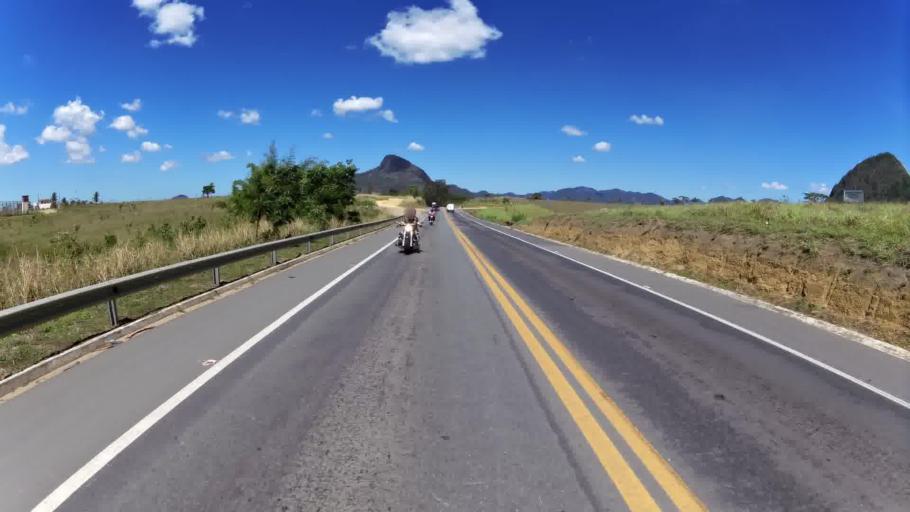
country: BR
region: Espirito Santo
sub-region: Viana
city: Viana
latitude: -20.4723
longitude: -40.4694
